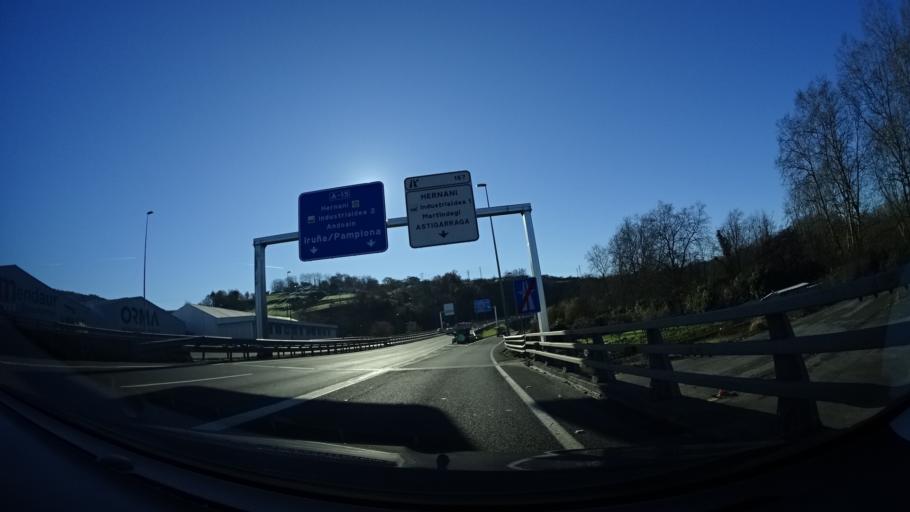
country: ES
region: Basque Country
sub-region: Provincia de Guipuzcoa
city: Astigarraga
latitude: 43.2711
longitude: -1.9575
